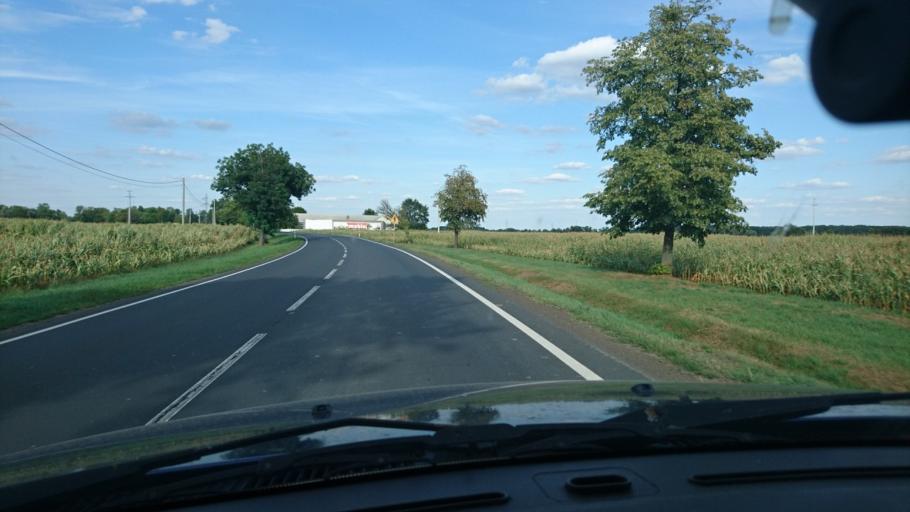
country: PL
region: Greater Poland Voivodeship
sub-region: Powiat krotoszynski
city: Kobylin
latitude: 51.7225
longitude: 17.2653
